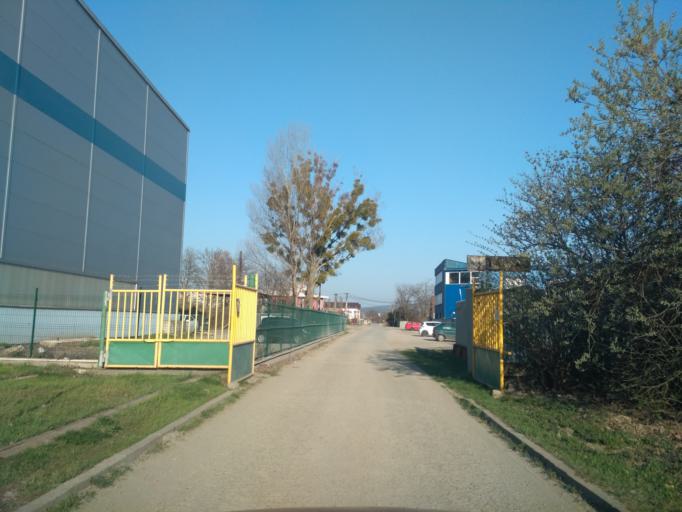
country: SK
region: Kosicky
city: Kosice
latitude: 48.6718
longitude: 21.2952
